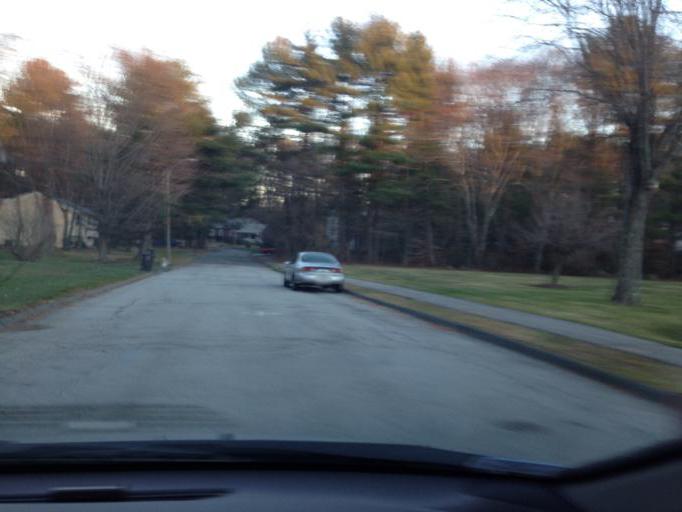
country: US
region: Massachusetts
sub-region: Middlesex County
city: Bedford
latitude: 42.4927
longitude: -71.2714
